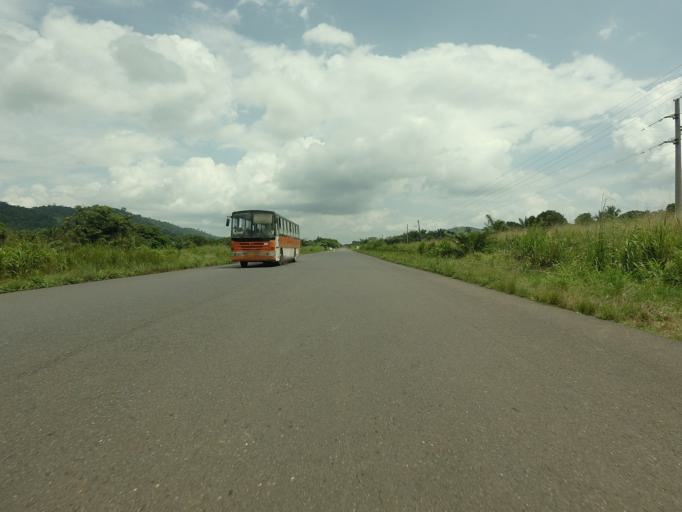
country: GH
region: Volta
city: Ho
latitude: 6.5102
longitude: 0.2144
